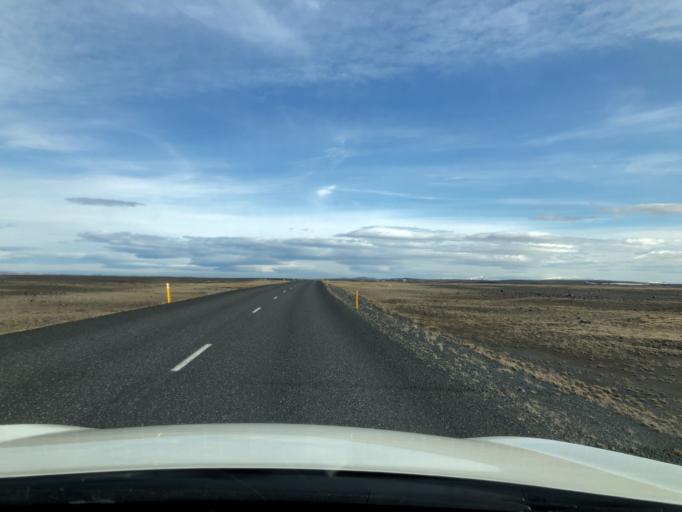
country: IS
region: Northeast
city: Laugar
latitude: 65.6682
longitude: -16.3724
